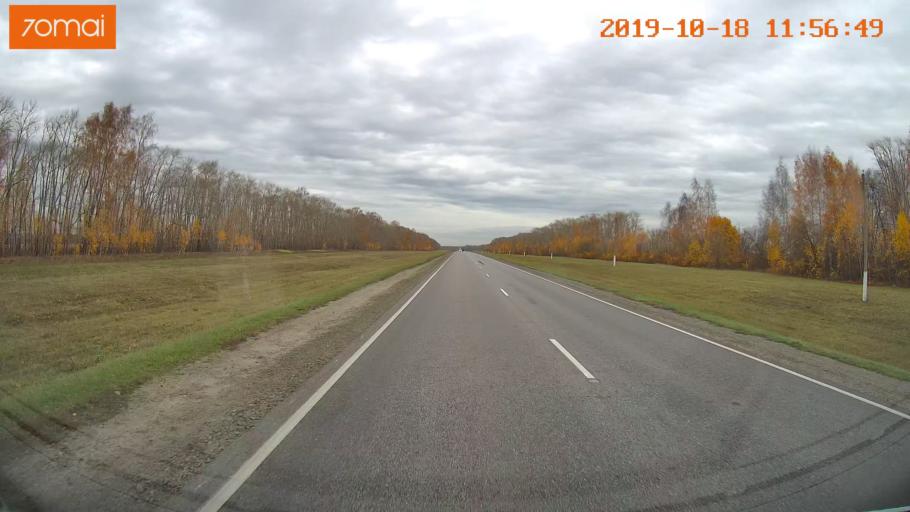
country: RU
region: Rjazan
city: Mikhaylov
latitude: 54.2659
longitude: 39.1265
